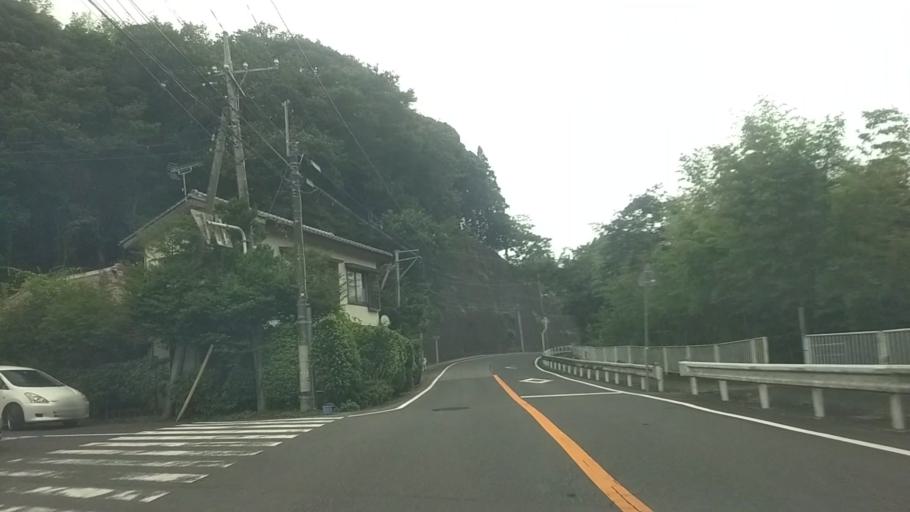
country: JP
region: Chiba
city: Katsuura
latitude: 35.2537
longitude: 140.2223
